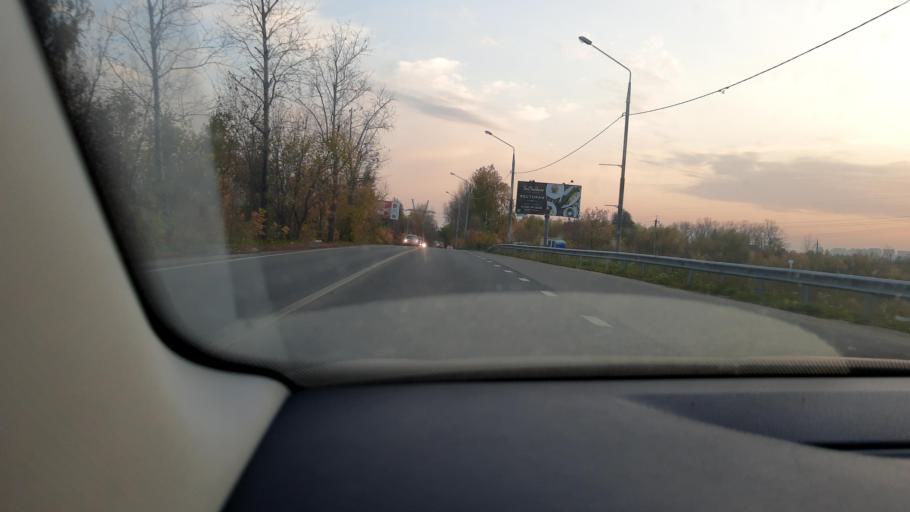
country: RU
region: Moskovskaya
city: Biryulevo Zapadnoye
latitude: 55.5706
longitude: 37.6497
